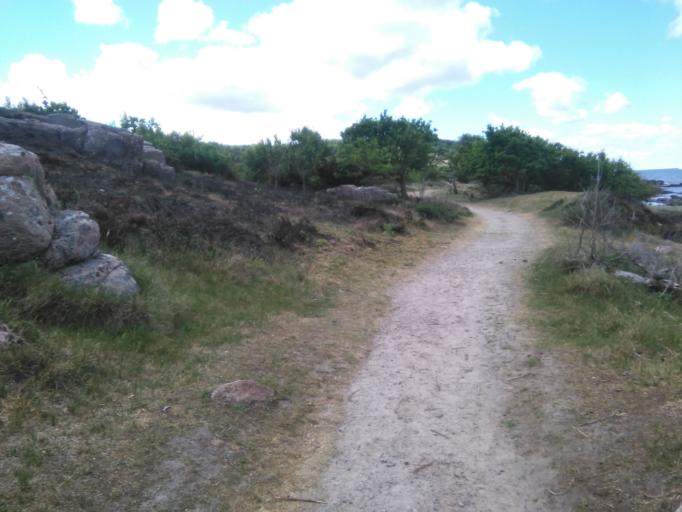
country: DK
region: Capital Region
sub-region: Bornholm Kommune
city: Ronne
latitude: 55.2953
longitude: 14.7657
